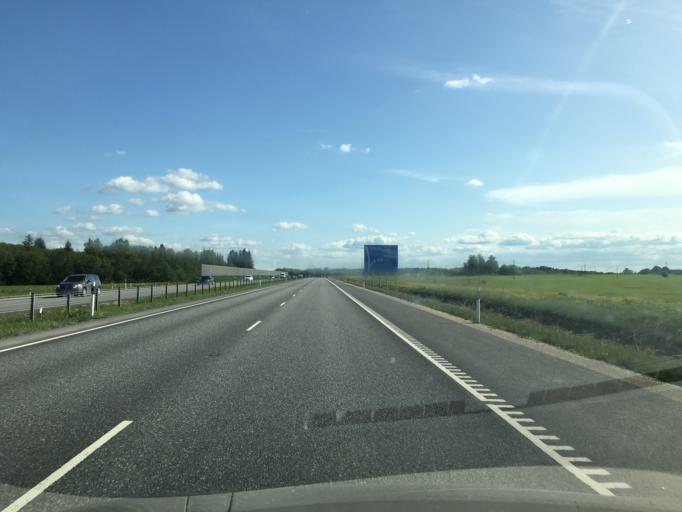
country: EE
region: Harju
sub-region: Rae vald
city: Vaida
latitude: 59.2072
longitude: 25.0389
